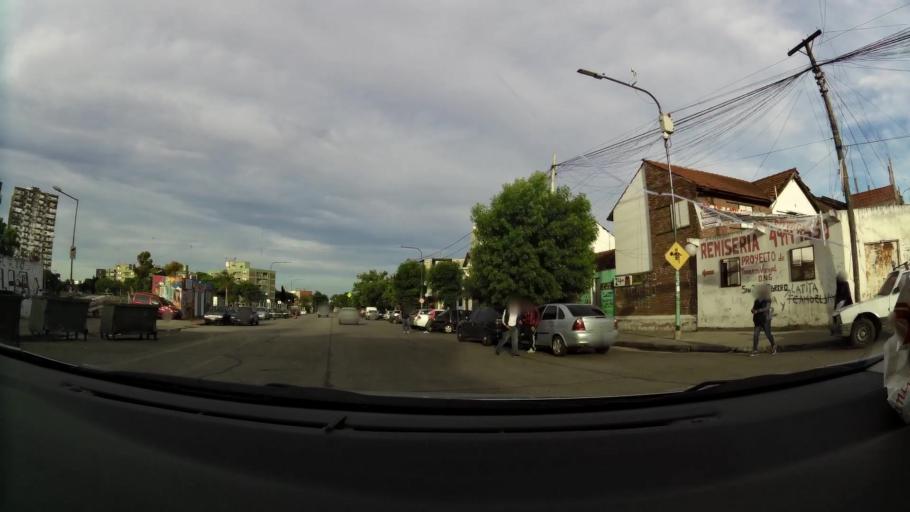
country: AR
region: Buenos Aires F.D.
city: Villa Lugano
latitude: -34.6473
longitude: -58.4374
